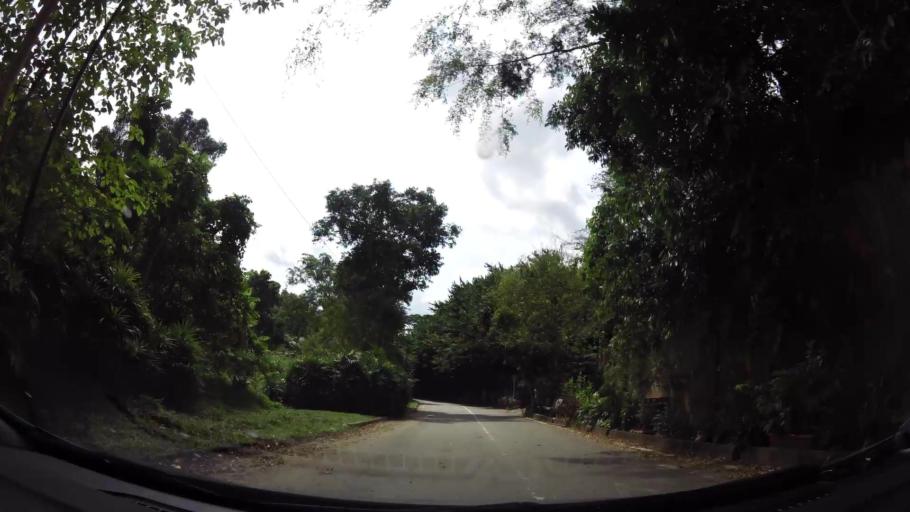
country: SG
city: Singapore
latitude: 1.3384
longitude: 103.7973
